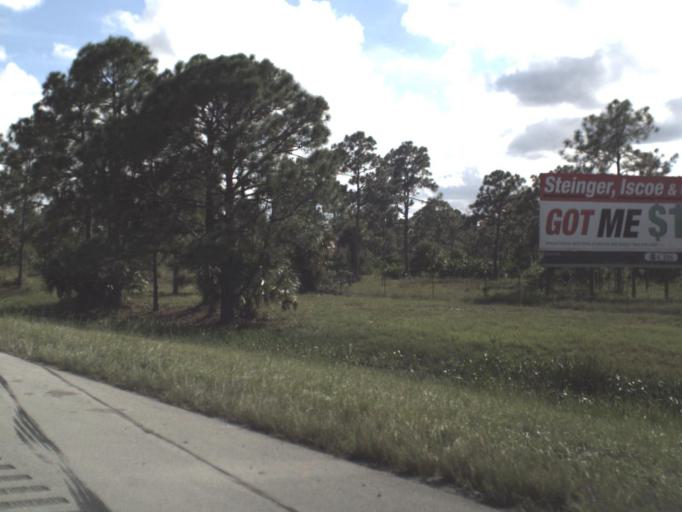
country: US
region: Florida
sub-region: Martin County
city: North River Shores
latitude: 27.1933
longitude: -80.3259
